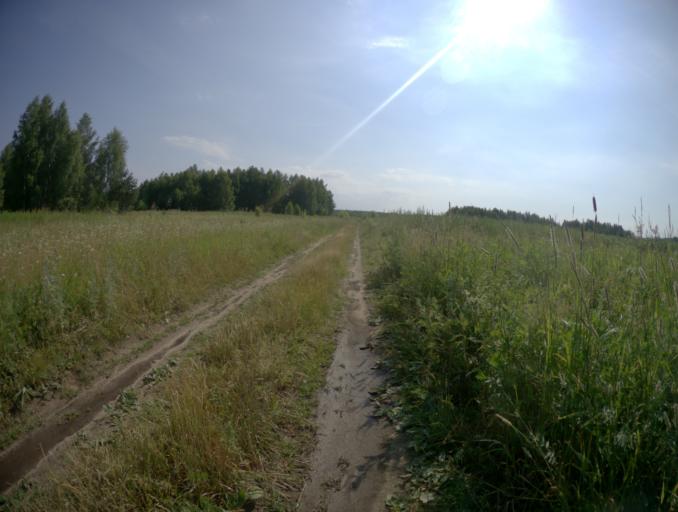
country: RU
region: Vladimir
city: Vyazniki
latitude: 56.3384
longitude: 42.1395
